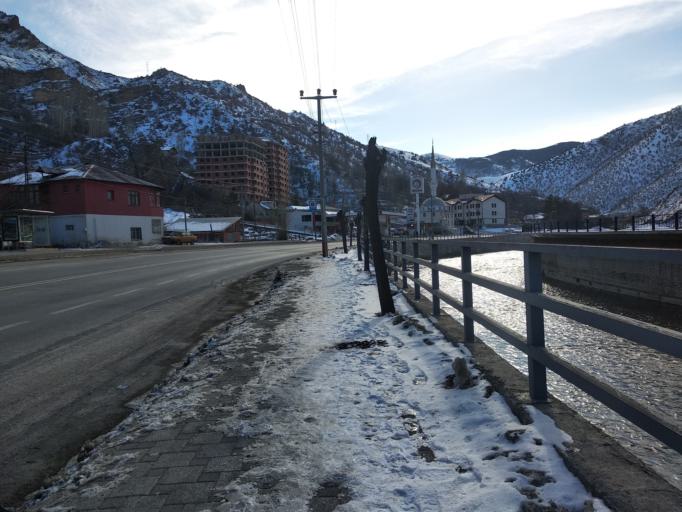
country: TR
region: Gumushane
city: Gumushkhane
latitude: 40.4460
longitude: 39.5029
